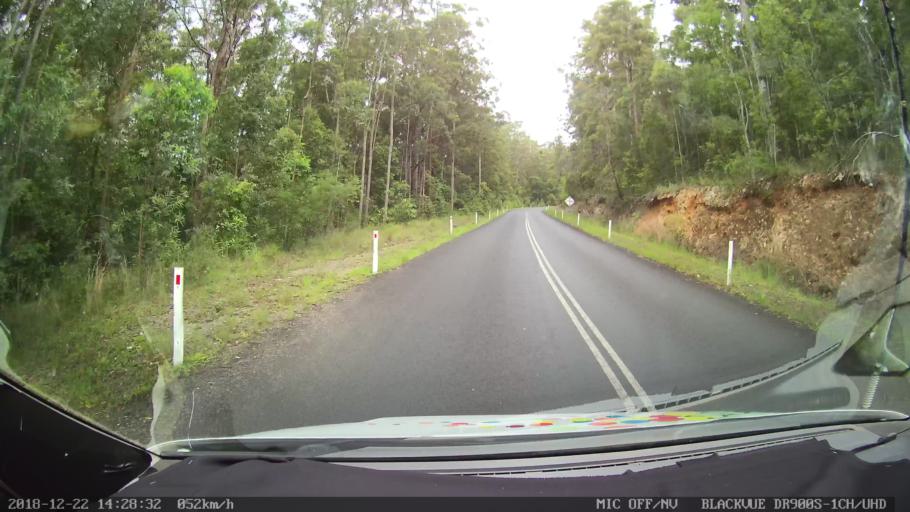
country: AU
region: New South Wales
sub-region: Bellingen
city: Dorrigo
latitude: -30.0735
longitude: 152.6366
